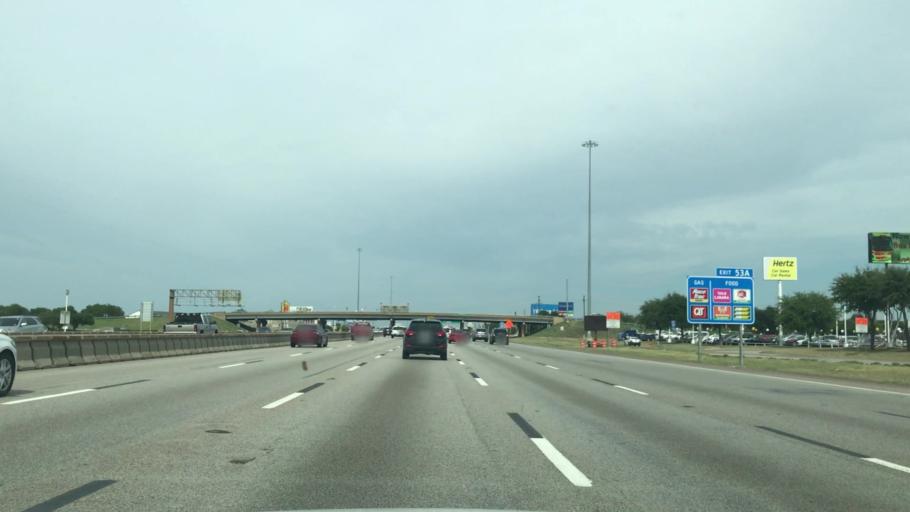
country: US
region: Texas
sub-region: Dallas County
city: Balch Springs
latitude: 32.7943
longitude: -96.6946
